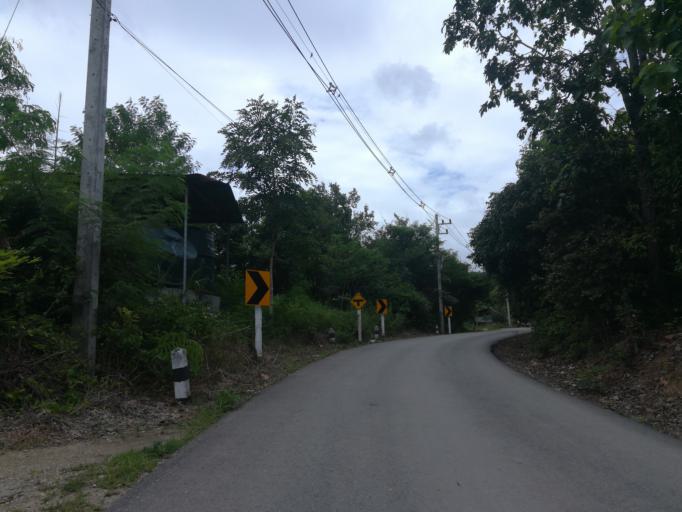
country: TH
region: Chiang Mai
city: Chom Thong
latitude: 18.4051
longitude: 98.6522
